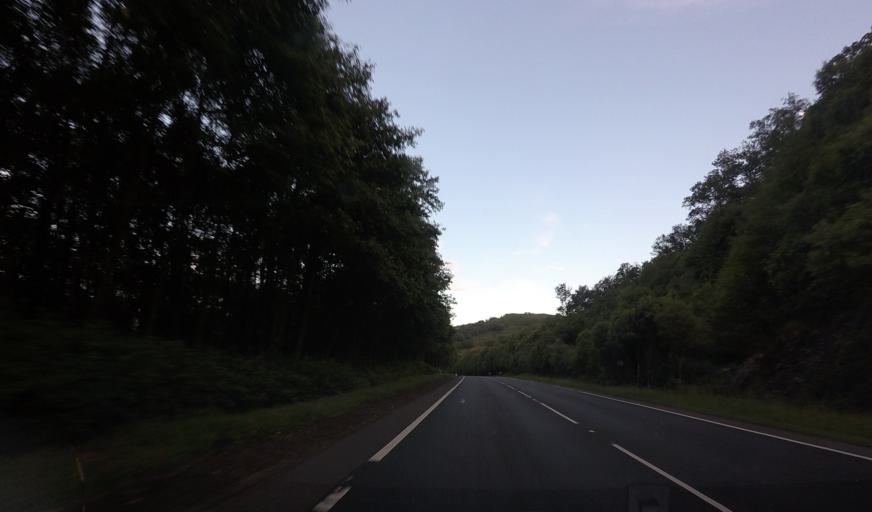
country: GB
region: Scotland
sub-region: Argyll and Bute
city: Garelochhead
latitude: 56.1731
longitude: -4.6827
